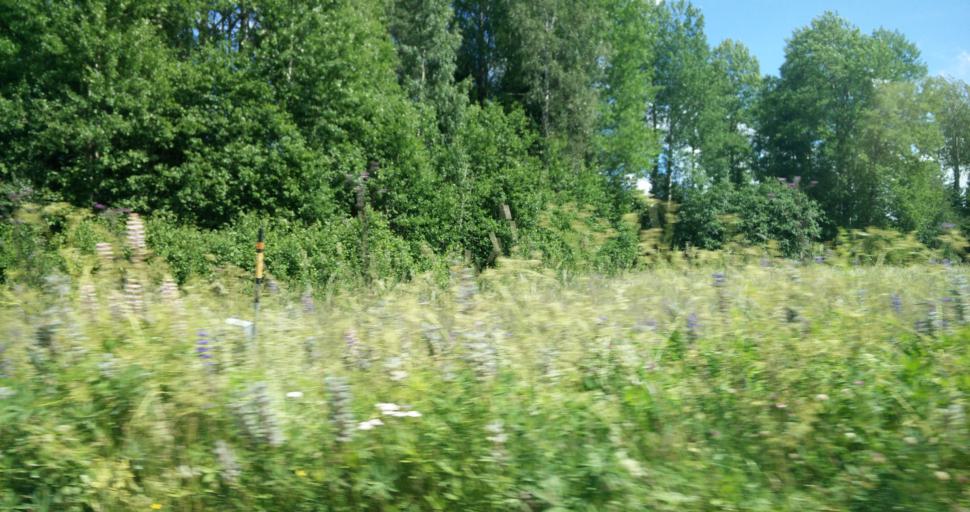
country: SE
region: Vaermland
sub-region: Hagfors Kommun
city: Hagfors
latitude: 60.0313
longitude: 13.6685
